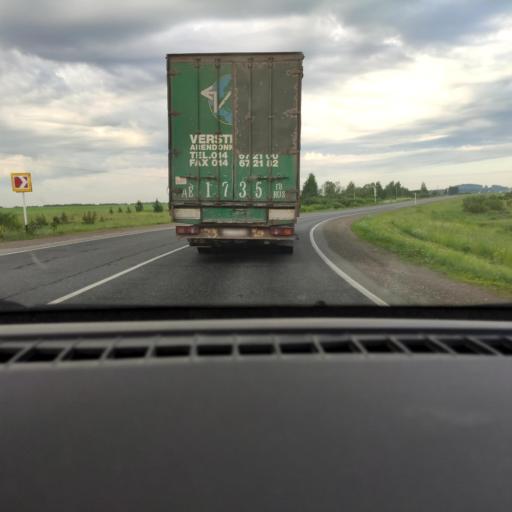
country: RU
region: Udmurtiya
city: Votkinsk
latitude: 57.3539
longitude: 54.4310
